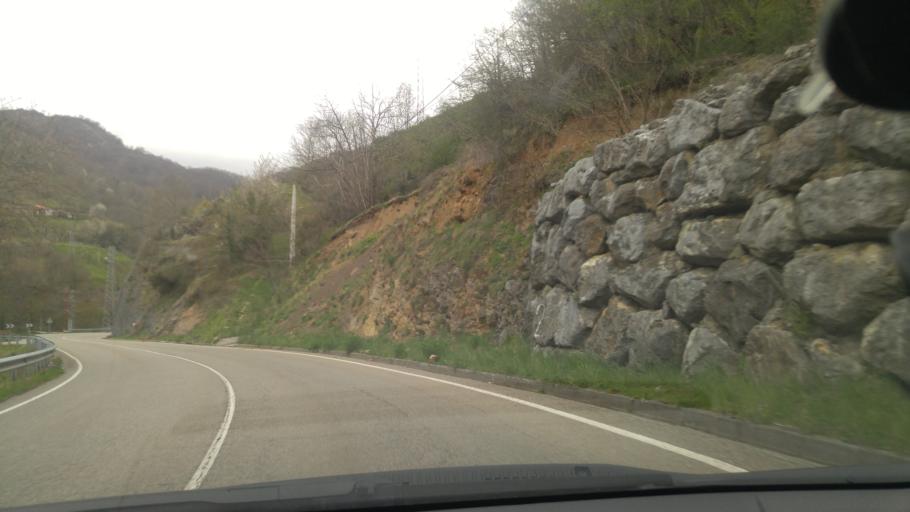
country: ES
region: Asturias
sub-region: Province of Asturias
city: Rio Aller
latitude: 43.1390
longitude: -5.5734
